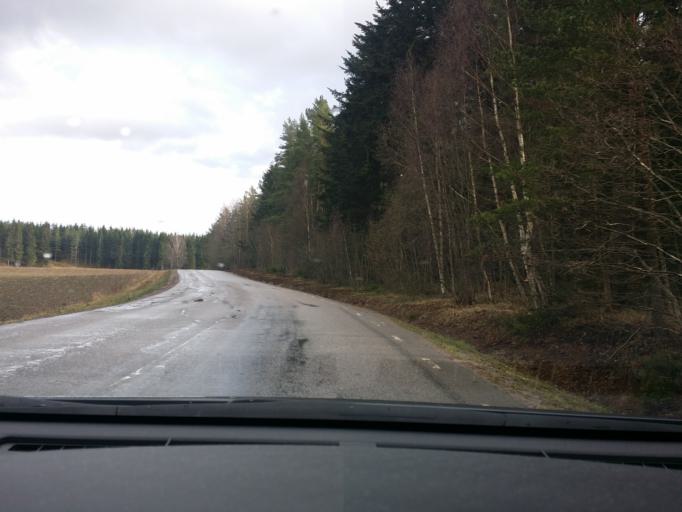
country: SE
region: Soedermanland
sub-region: Eskilstuna Kommun
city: Arla
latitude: 59.3183
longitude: 16.6800
